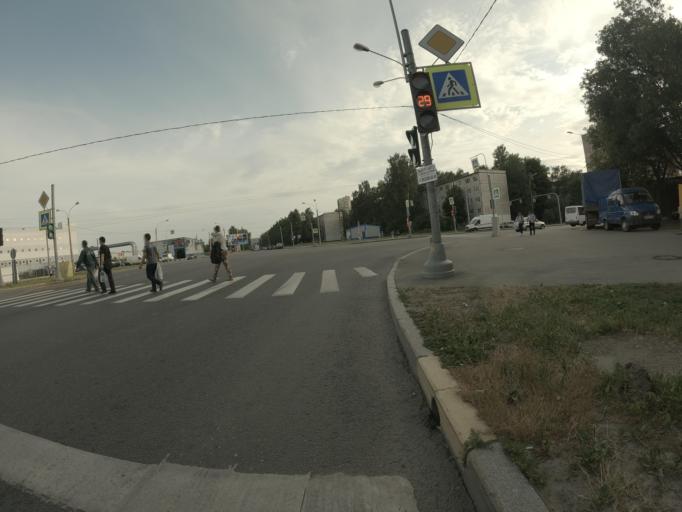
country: RU
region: Leningrad
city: Rybatskoye
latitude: 59.8794
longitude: 30.4829
